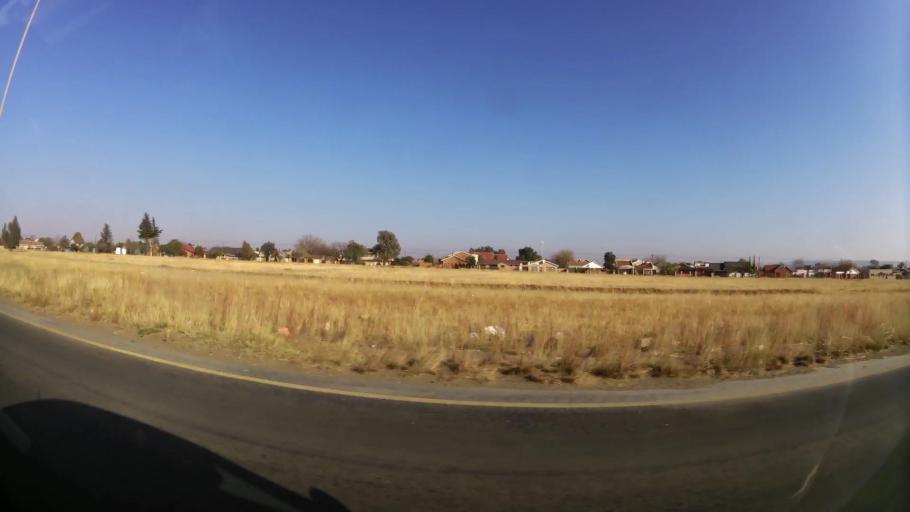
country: ZA
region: Orange Free State
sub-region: Mangaung Metropolitan Municipality
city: Bloemfontein
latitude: -29.1433
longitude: 26.2662
